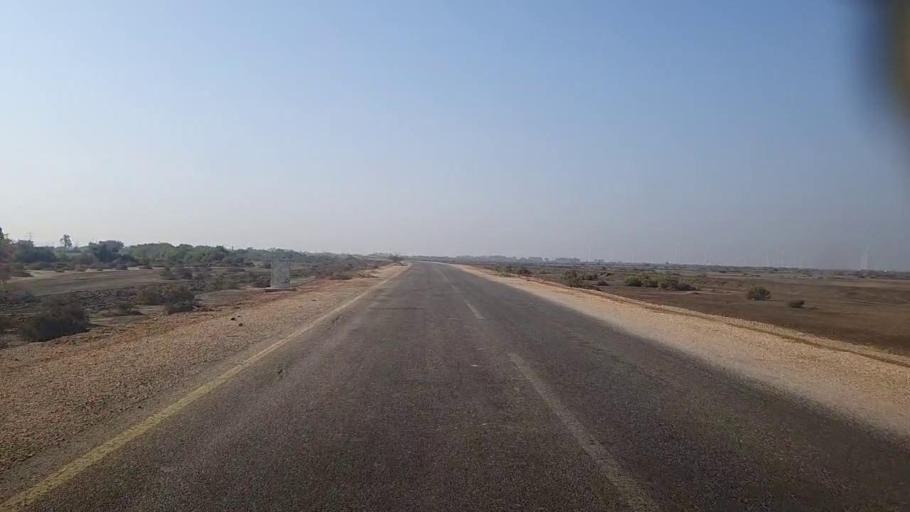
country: PK
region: Sindh
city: Gharo
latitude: 24.6961
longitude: 67.5252
